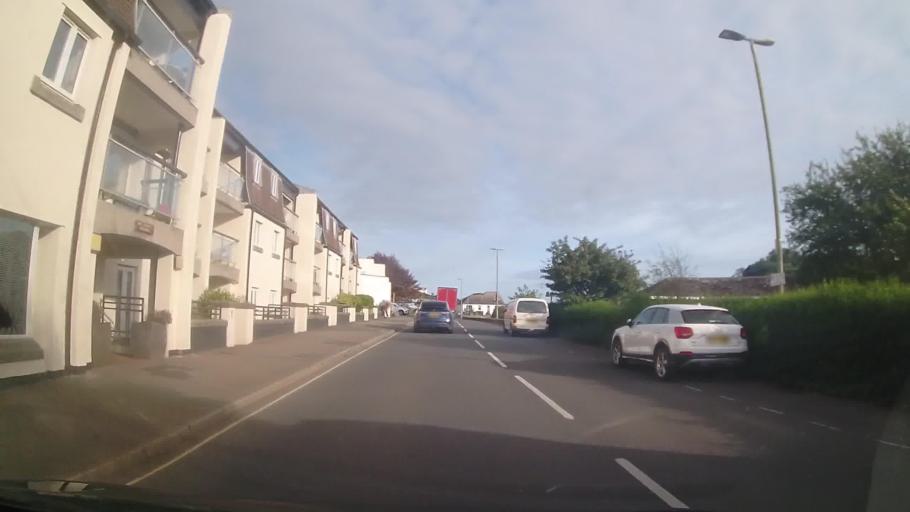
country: GB
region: England
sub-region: Devon
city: Kingsbridge
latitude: 50.2806
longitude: -3.7743
